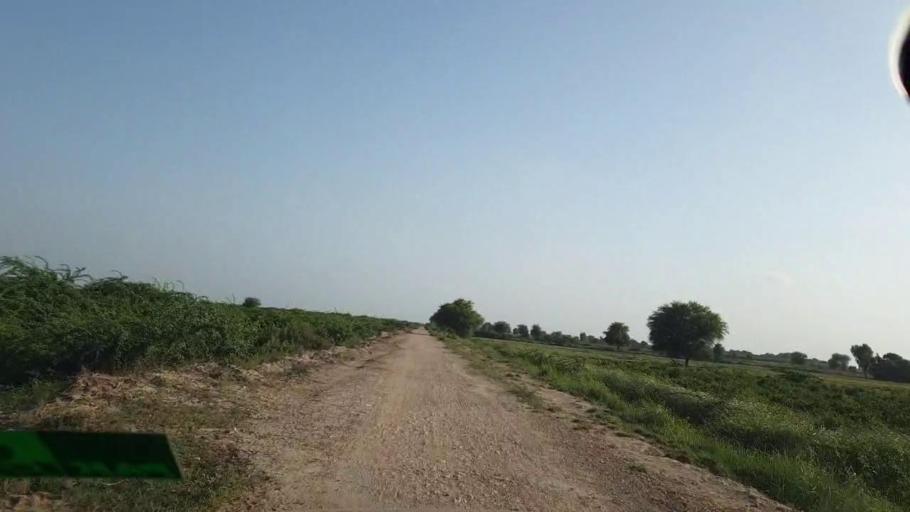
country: PK
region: Sindh
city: Naukot
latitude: 24.7253
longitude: 69.2517
